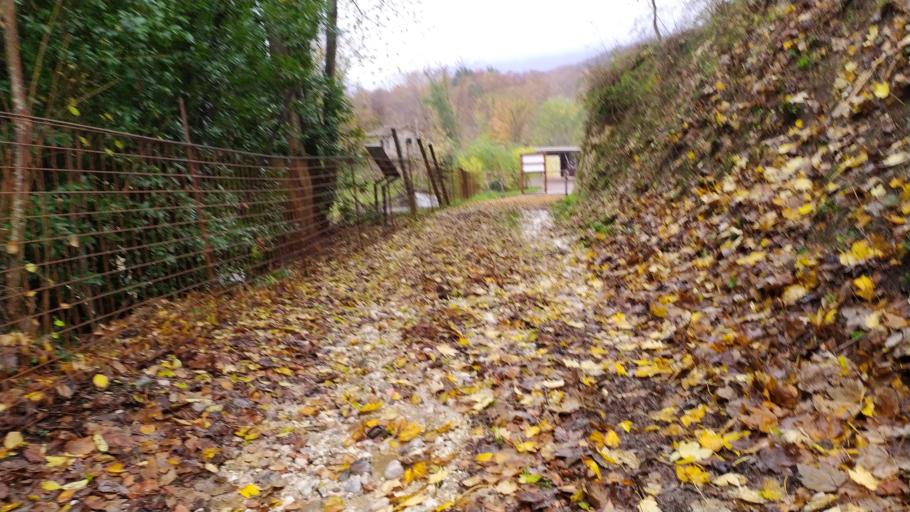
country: IT
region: Friuli Venezia Giulia
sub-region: Provincia di Pordenone
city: Pinzano al Tagliamento
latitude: 46.1845
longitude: 12.9447
